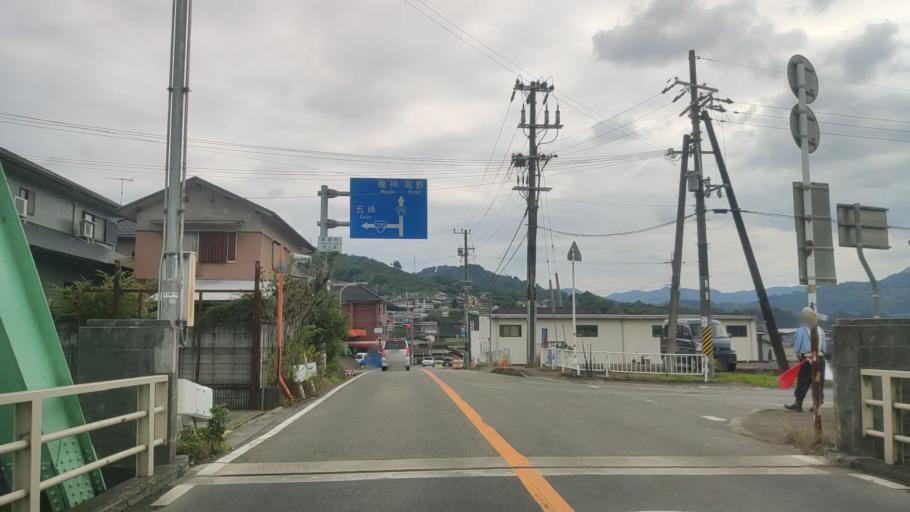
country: JP
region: Wakayama
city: Hashimoto
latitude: 34.2980
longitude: 135.5781
